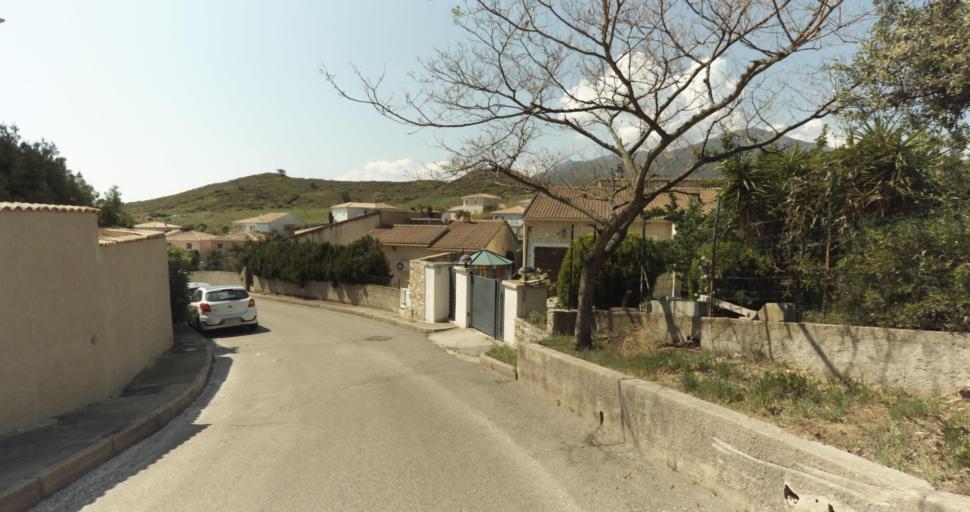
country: FR
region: Corsica
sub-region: Departement de la Haute-Corse
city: Biguglia
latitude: 42.6150
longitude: 9.4276
